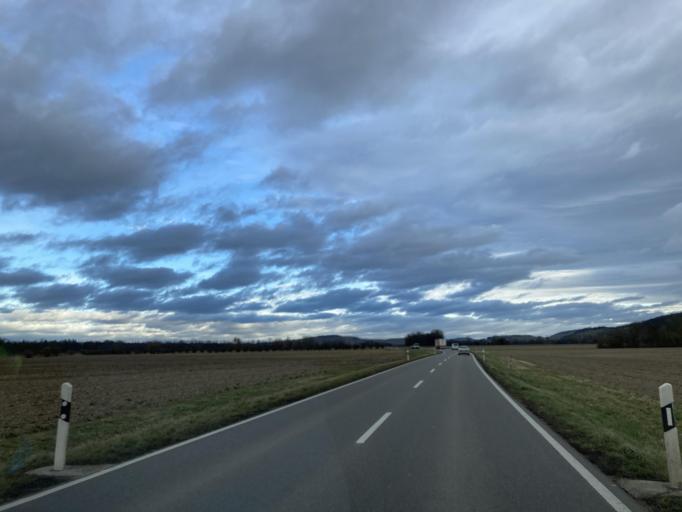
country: DE
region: Baden-Wuerttemberg
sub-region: Freiburg Region
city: Breisach am Rhein
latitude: 48.0563
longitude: 7.5930
